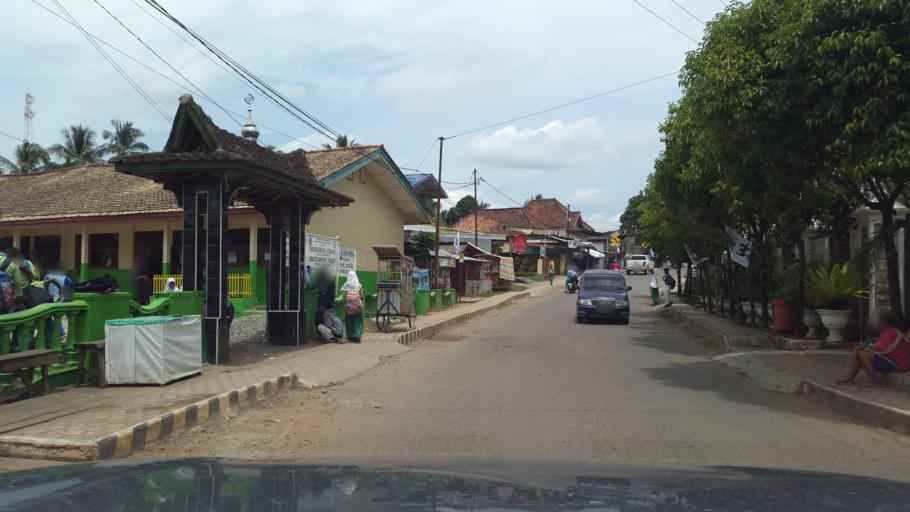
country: ID
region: South Sumatra
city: Gunungmegang Dalam
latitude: -3.2755
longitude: 103.8307
